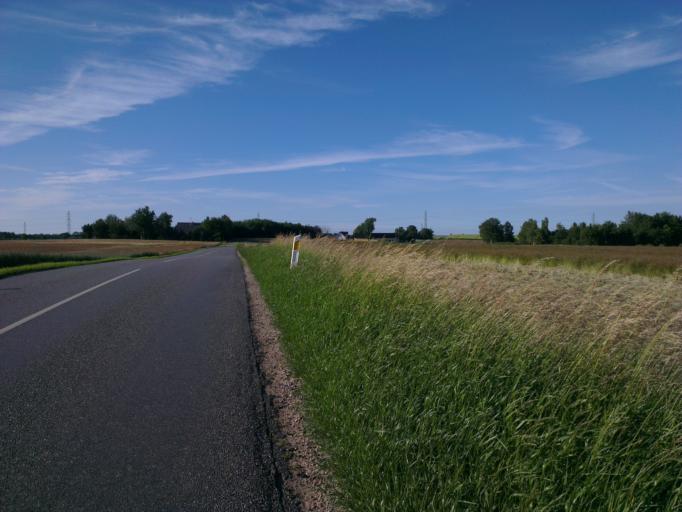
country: DK
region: Capital Region
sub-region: Frederikssund Kommune
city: Skibby
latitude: 55.7903
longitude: 12.0116
